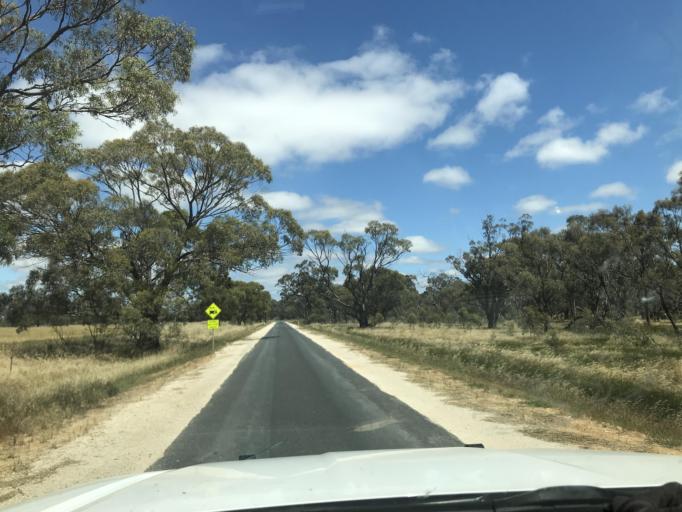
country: AU
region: South Australia
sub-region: Tatiara
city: Bordertown
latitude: -36.3086
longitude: 141.0448
